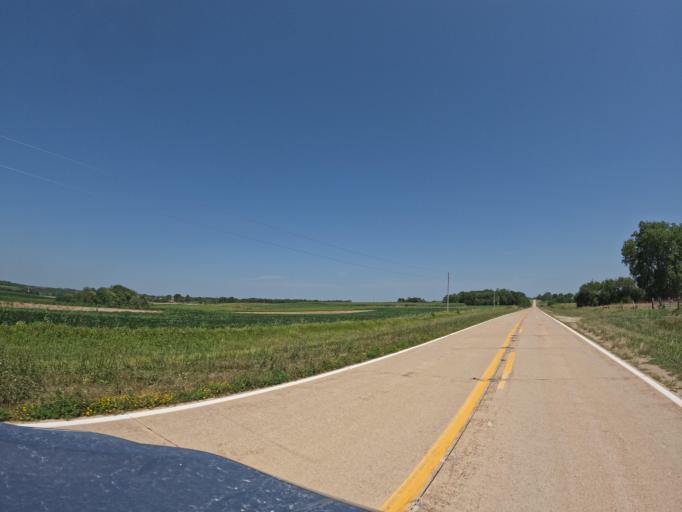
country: US
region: Iowa
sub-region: Henry County
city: Mount Pleasant
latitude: 40.8701
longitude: -91.5601
